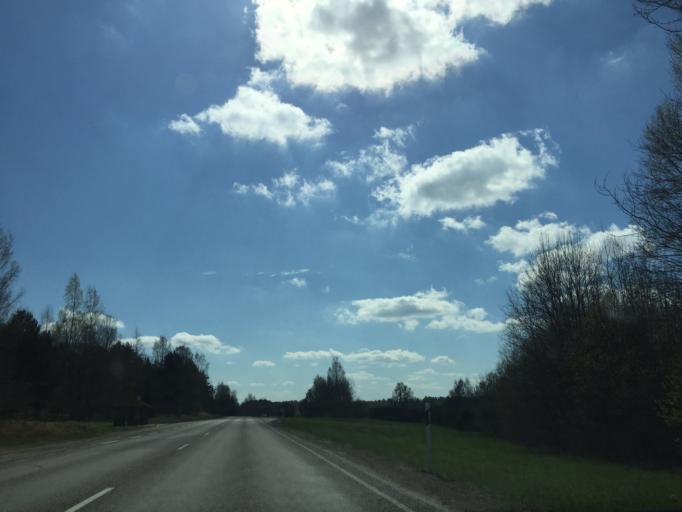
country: EE
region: Tartu
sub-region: Elva linn
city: Elva
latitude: 58.0943
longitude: 26.2270
